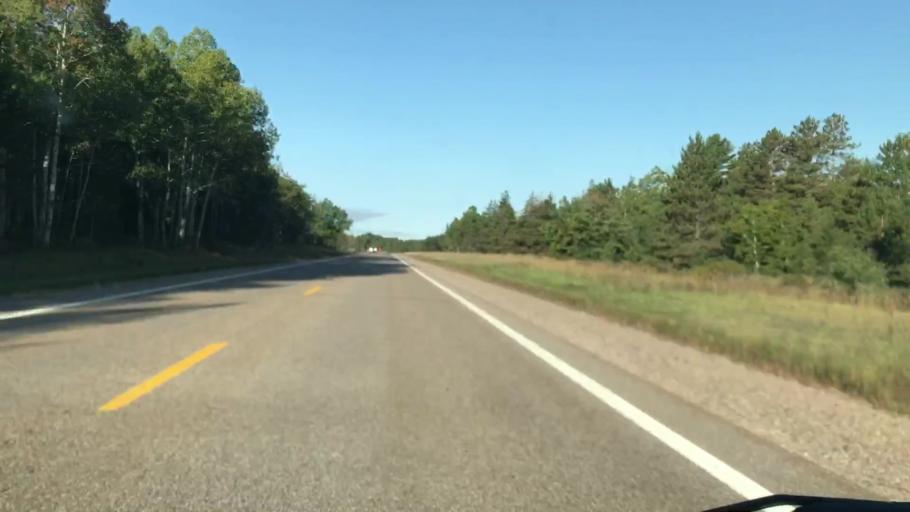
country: US
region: Michigan
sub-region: Mackinac County
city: Saint Ignace
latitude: 46.3584
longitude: -84.8723
